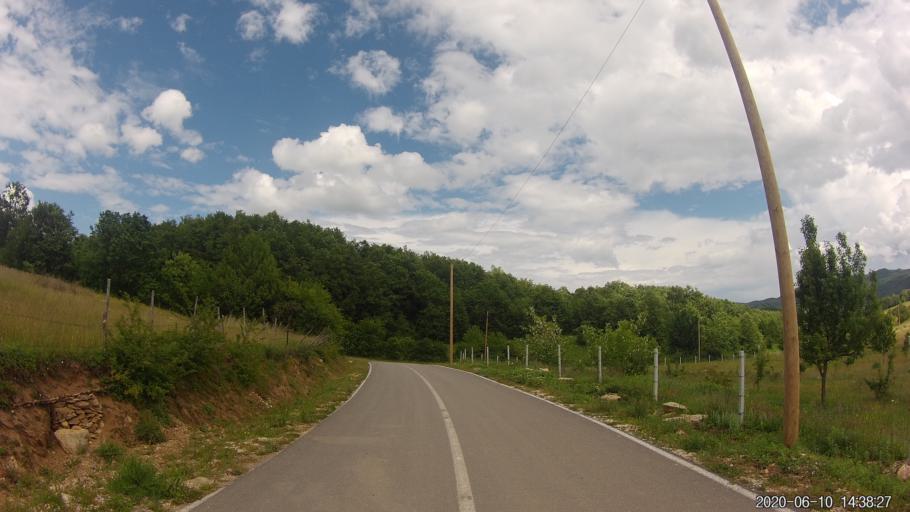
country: XK
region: Prizren
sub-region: Komuna e Therandes
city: Budakovo
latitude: 42.4043
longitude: 20.9410
